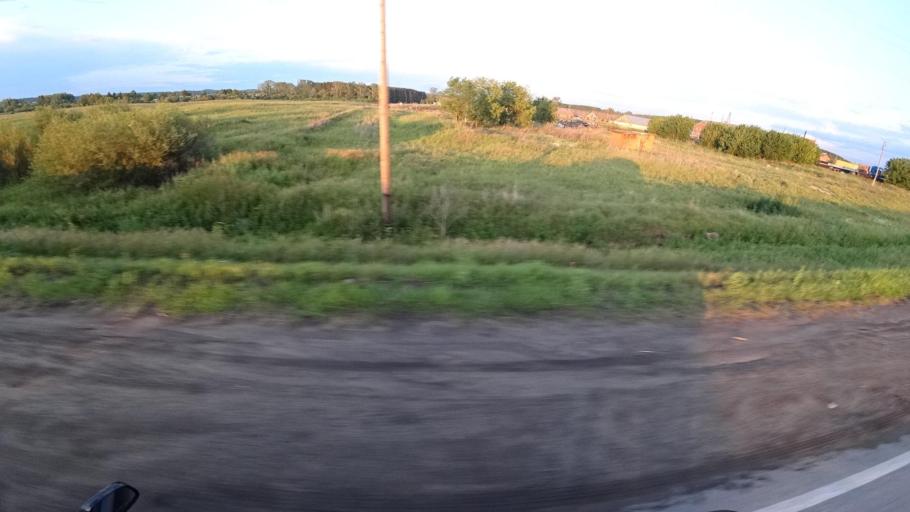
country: RU
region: Sverdlovsk
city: Kamyshlov
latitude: 56.8710
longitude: 62.7112
